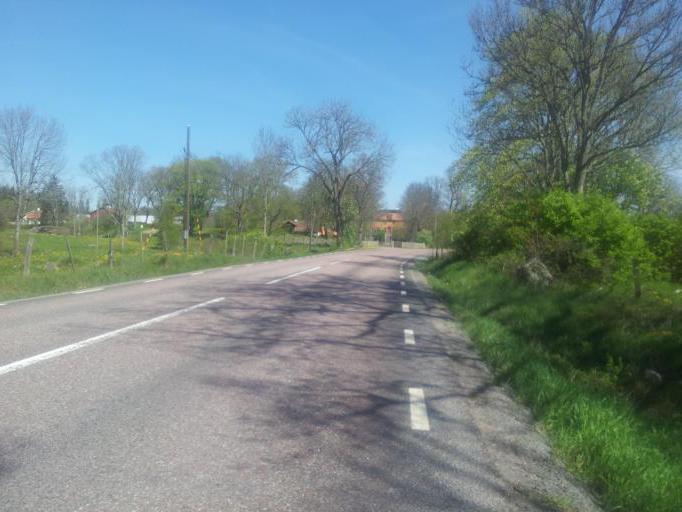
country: SE
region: Uppsala
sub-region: Knivsta Kommun
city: Knivsta
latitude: 59.8826
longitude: 17.9722
